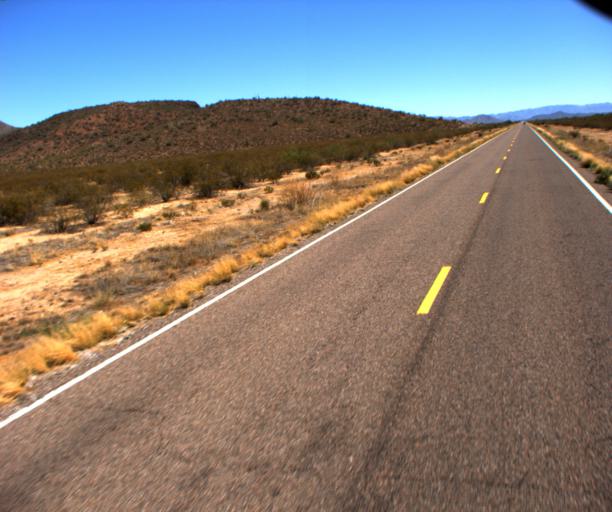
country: US
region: Arizona
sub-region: Yavapai County
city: Congress
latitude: 34.0054
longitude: -113.1150
